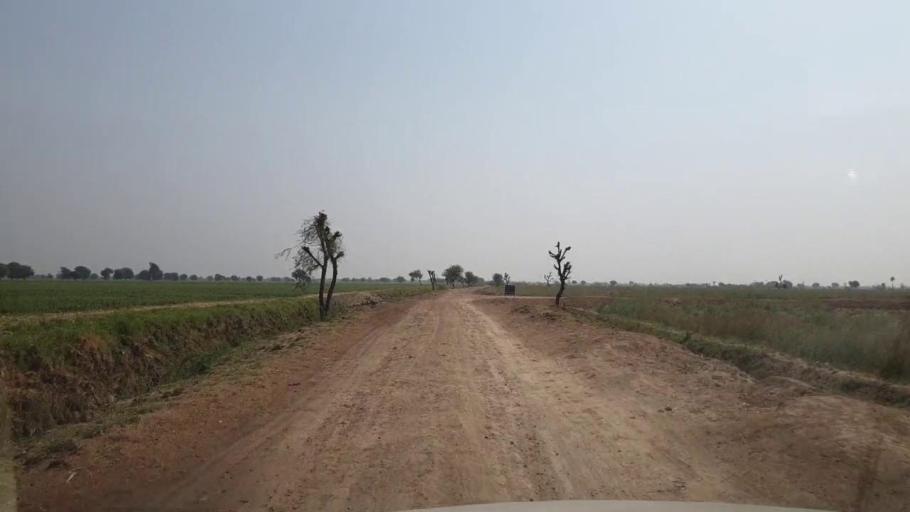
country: PK
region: Sindh
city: Chor
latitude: 25.4567
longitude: 69.6810
